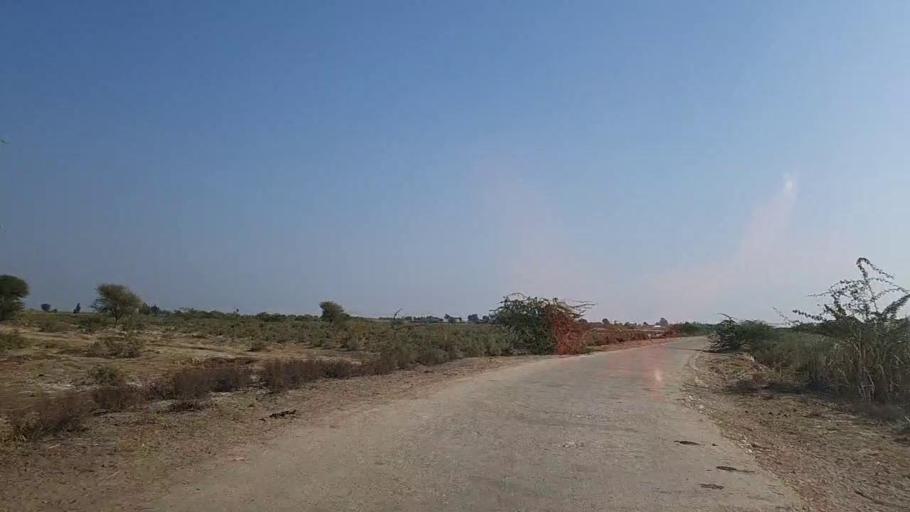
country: PK
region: Sindh
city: Tando Mittha Khan
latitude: 25.9363
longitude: 69.0581
